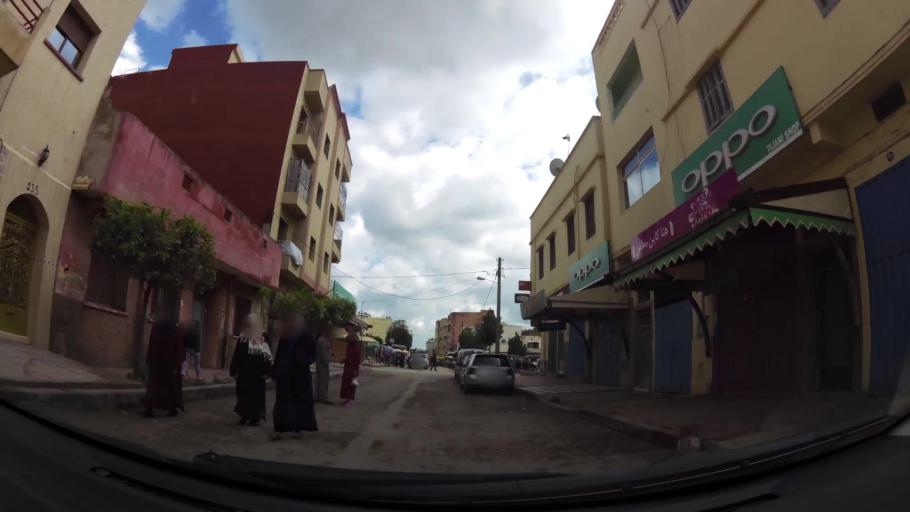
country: MA
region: Chaouia-Ouardigha
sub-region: Settat Province
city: Berrechid
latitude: 33.2671
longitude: -7.5870
